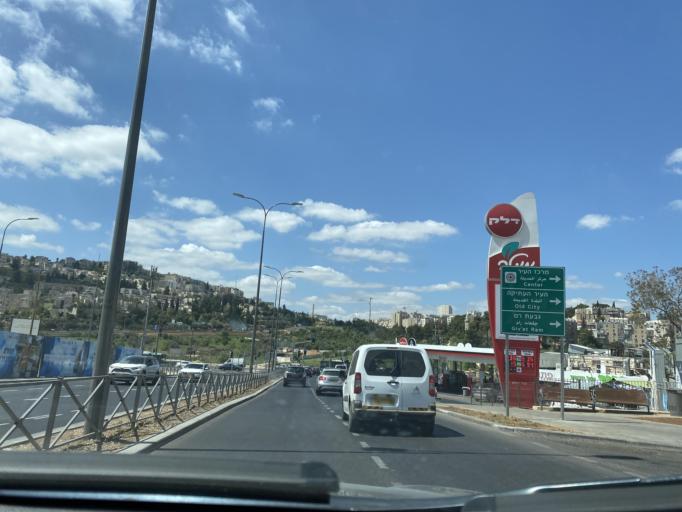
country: IL
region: Jerusalem
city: Jerusalem
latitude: 31.7566
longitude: 35.1982
